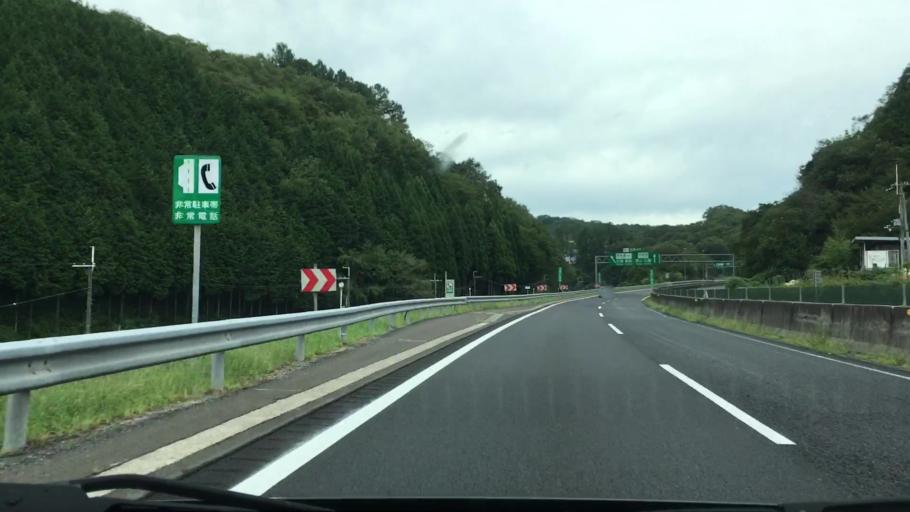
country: JP
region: Hyogo
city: Yamazakicho-nakabirose
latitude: 35.0252
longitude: 134.3956
